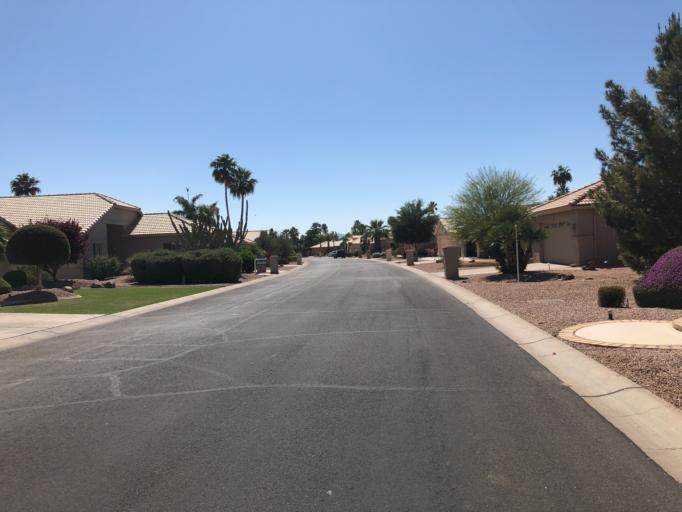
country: US
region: Arizona
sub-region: Maricopa County
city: Sun Lakes
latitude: 33.2300
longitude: -111.8770
